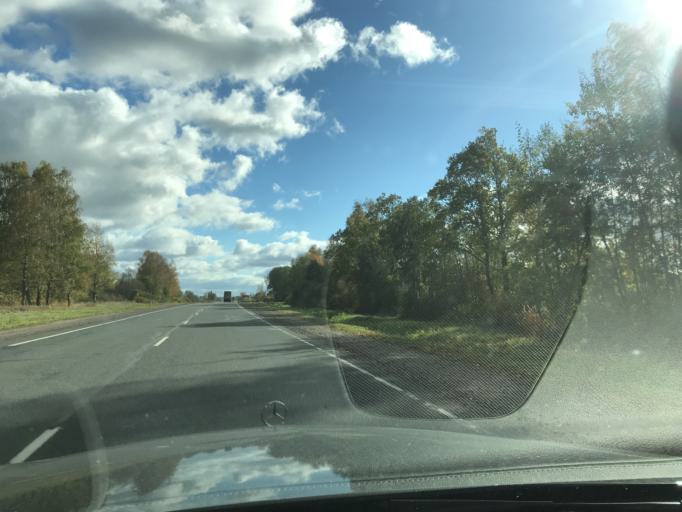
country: RU
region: Pskov
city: Ostrov
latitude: 57.2743
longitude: 28.4046
